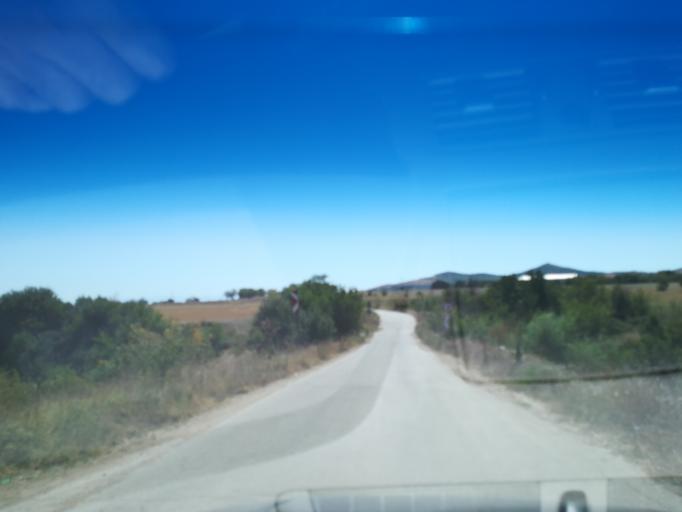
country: BG
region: Pazardzhik
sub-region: Obshtina Pazardzhik
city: Pazardzhik
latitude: 42.3528
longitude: 24.3998
